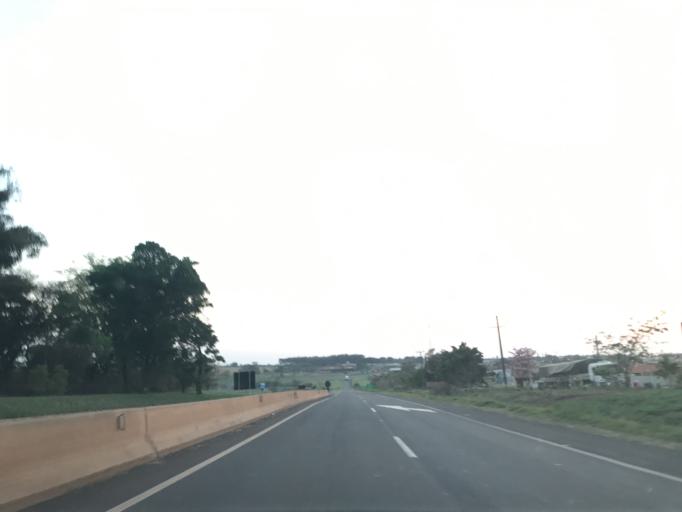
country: BR
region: Sao Paulo
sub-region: Assis
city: Assis
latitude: -22.6412
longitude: -50.4384
